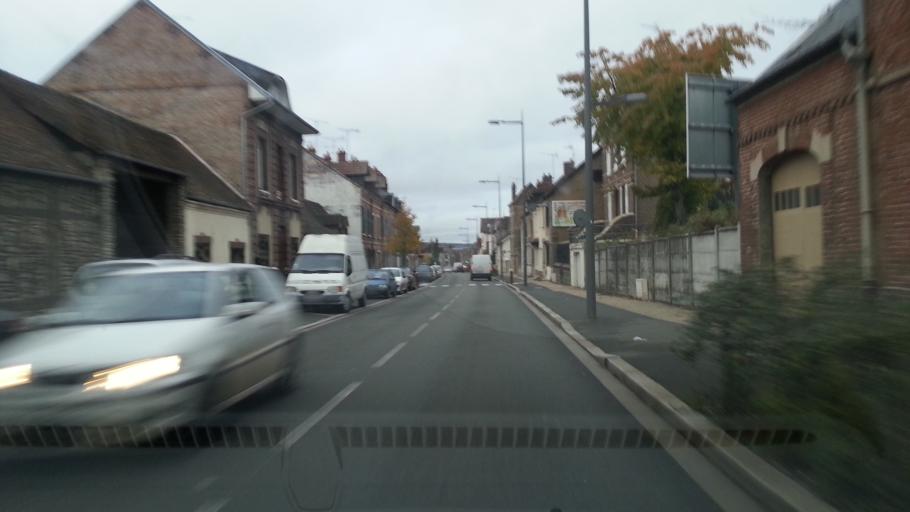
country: FR
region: Picardie
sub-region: Departement de l'Oise
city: Beauvais
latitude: 49.4325
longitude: 2.0991
